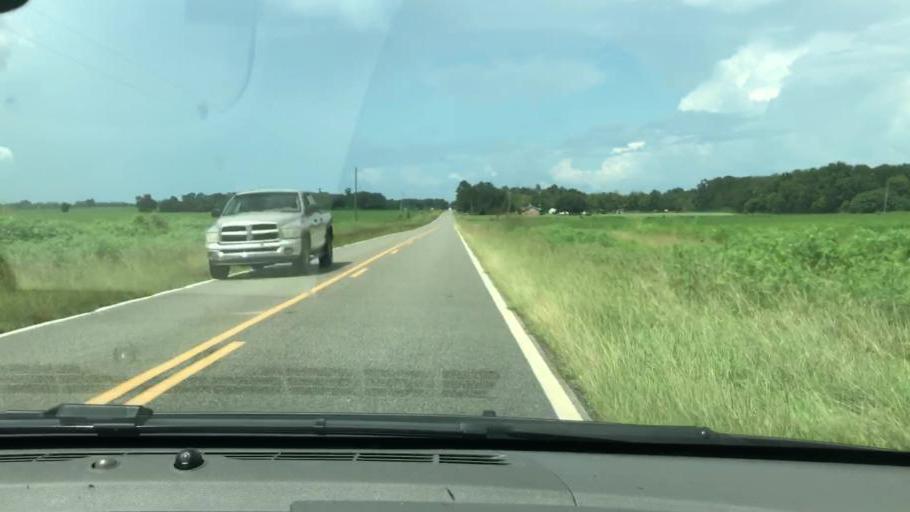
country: US
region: Georgia
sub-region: Seminole County
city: Donalsonville
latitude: 31.1022
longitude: -84.9961
